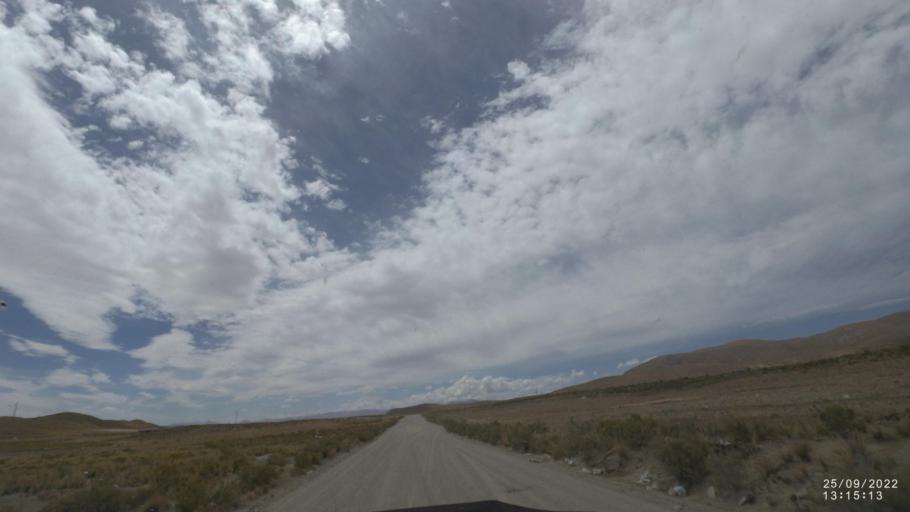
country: BO
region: Oruro
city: Oruro
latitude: -17.9306
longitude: -67.0409
